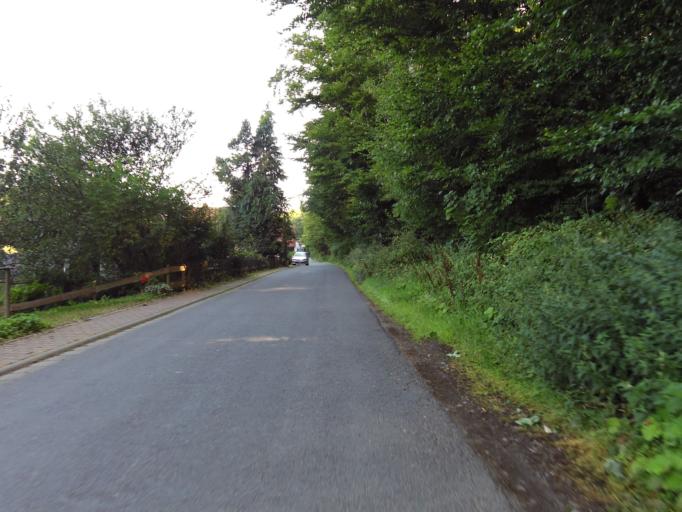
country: DE
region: Hesse
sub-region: Regierungsbezirk Darmstadt
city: Lindenfels
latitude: 49.6831
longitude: 8.7252
